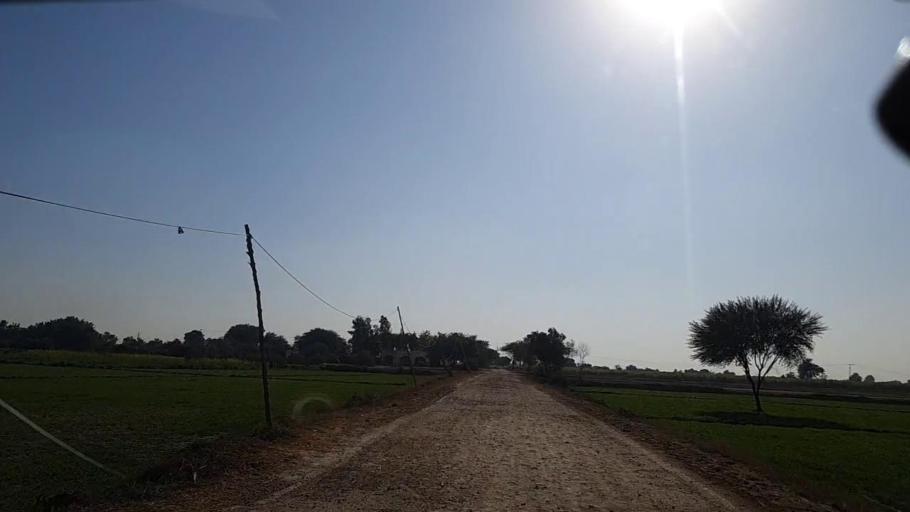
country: PK
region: Sindh
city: Khanpur
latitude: 27.7849
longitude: 69.3682
